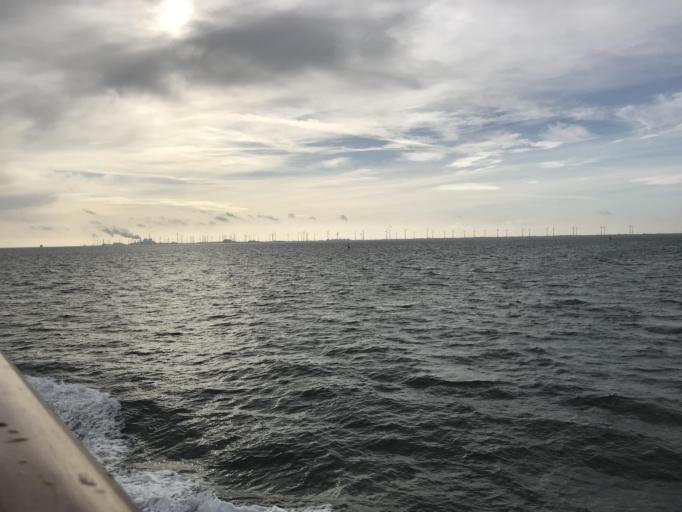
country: DE
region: Lower Saxony
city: Borkum
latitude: 53.5233
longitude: 6.7715
